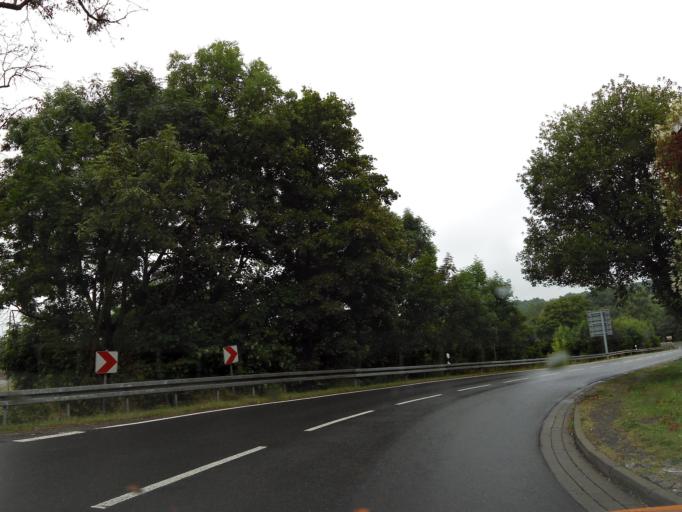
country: DE
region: Saxony-Anhalt
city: Harzgerode
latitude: 51.6408
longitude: 11.1359
